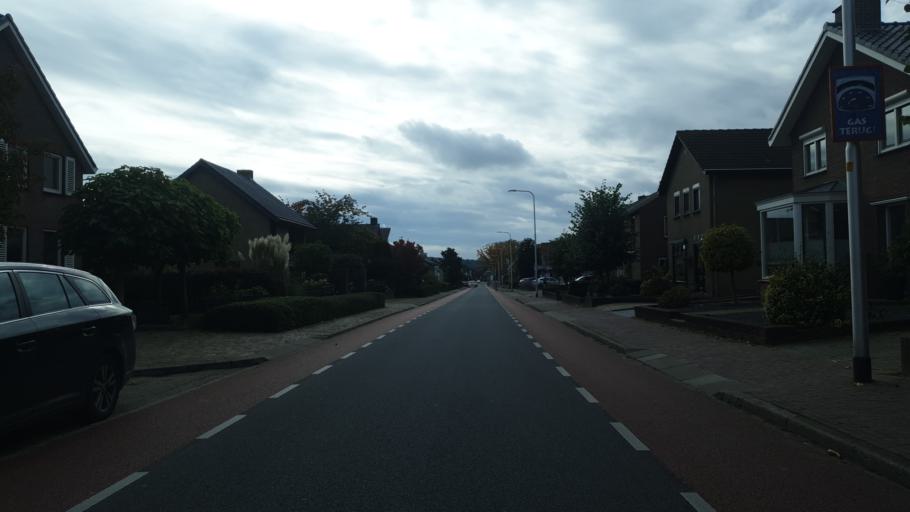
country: NL
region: Gelderland
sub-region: Gemeente Groesbeek
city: Bredeweg
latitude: 51.7617
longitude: 5.9410
